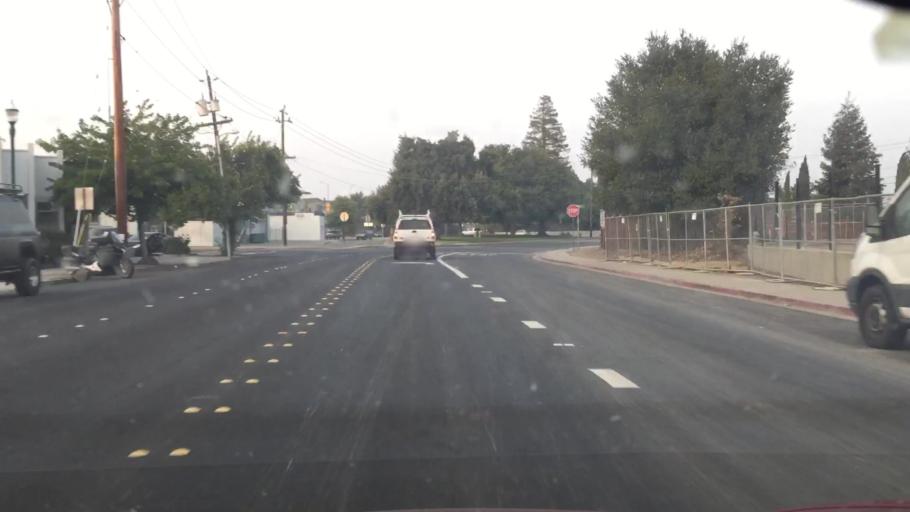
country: US
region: California
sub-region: Alameda County
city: Livermore
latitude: 37.6839
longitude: -121.7617
